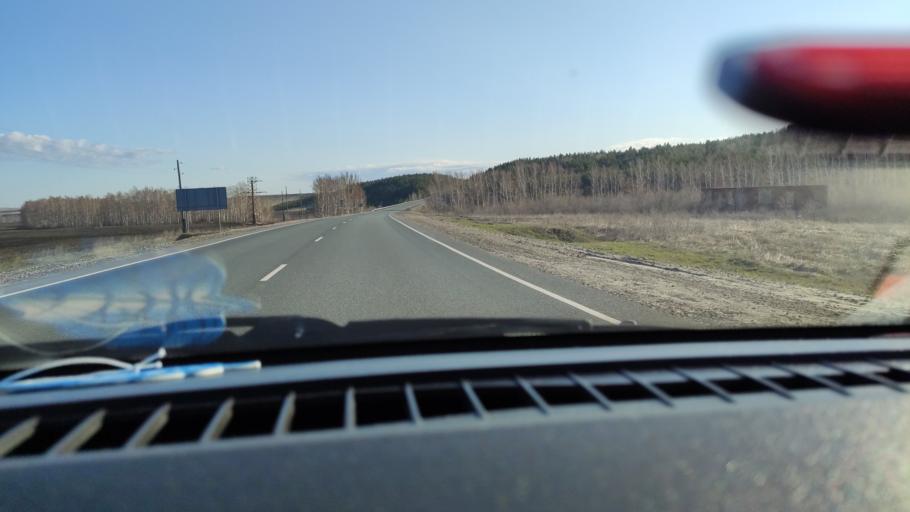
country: RU
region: Saratov
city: Khvalynsk
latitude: 52.5272
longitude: 48.0250
